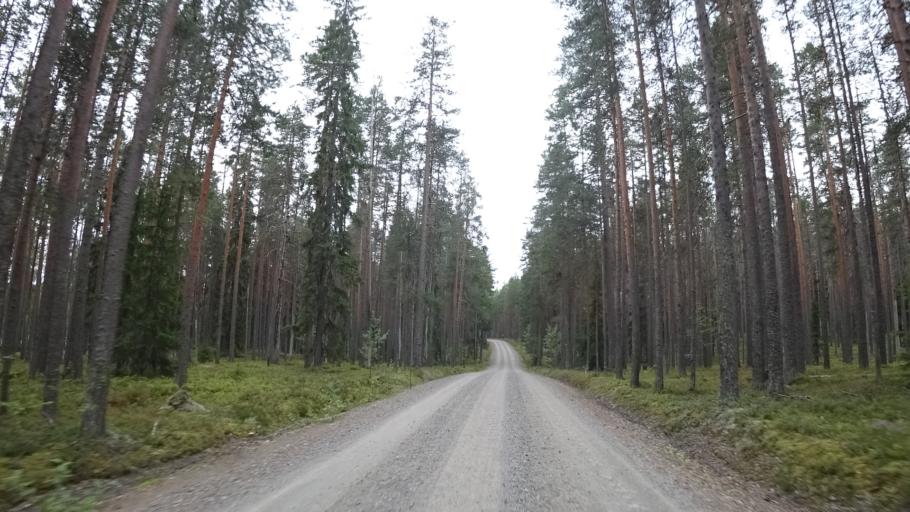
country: FI
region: North Karelia
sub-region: Joensuu
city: Ilomantsi
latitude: 62.5880
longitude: 31.1698
